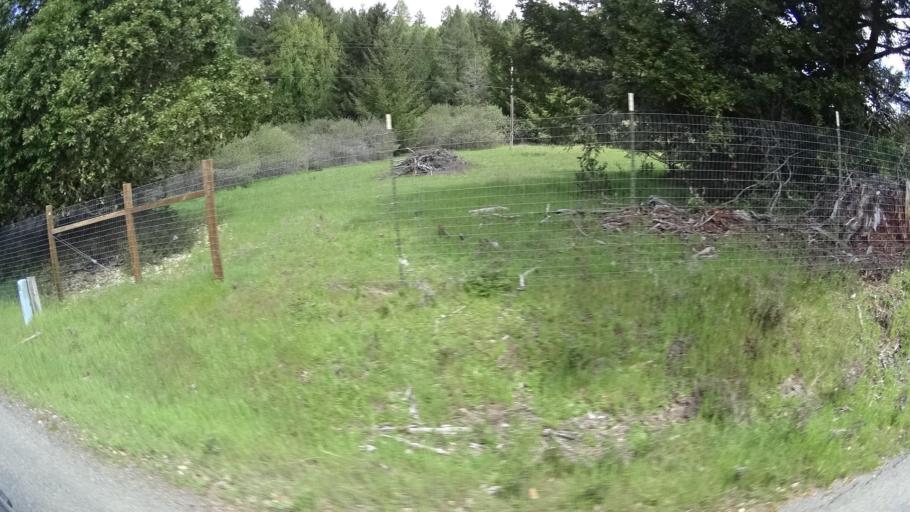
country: US
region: California
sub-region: Humboldt County
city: Redway
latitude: 40.0456
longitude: -123.9585
